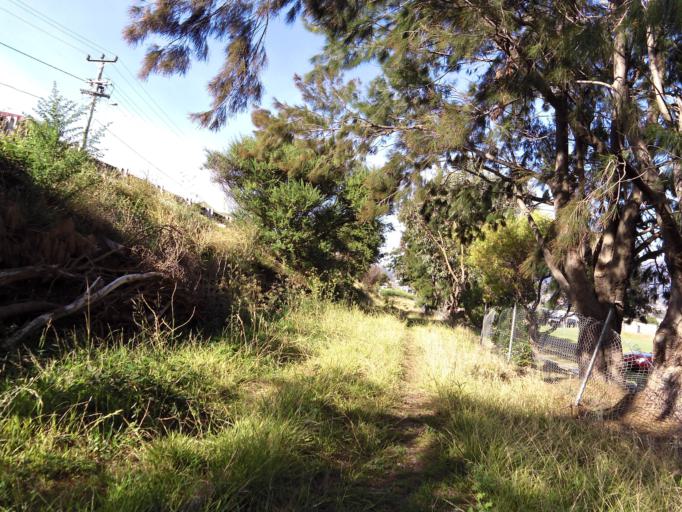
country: AU
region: Tasmania
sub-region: Glenorchy
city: Lutana
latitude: -42.8353
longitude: 147.3043
